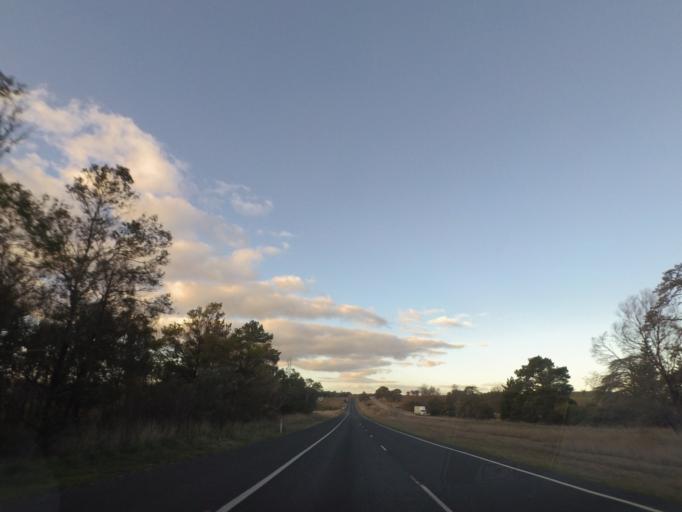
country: AU
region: New South Wales
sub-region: Yass Valley
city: Yass
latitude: -34.7705
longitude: 148.7455
